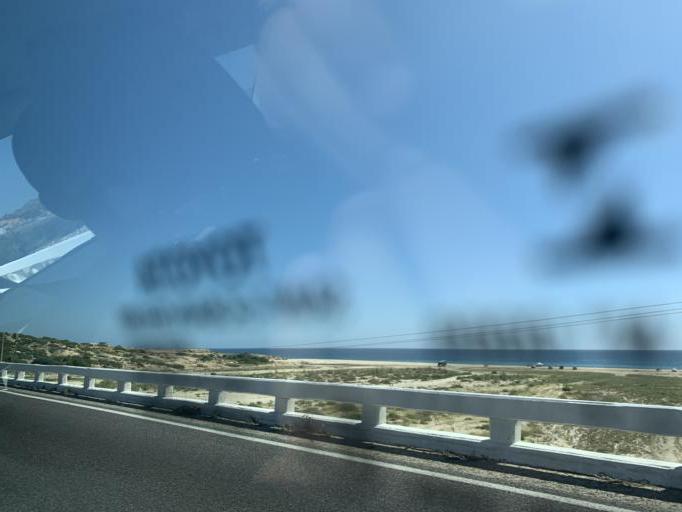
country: MX
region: Baja California Sur
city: Cabo San Lucas
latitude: 22.9616
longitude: -109.8020
